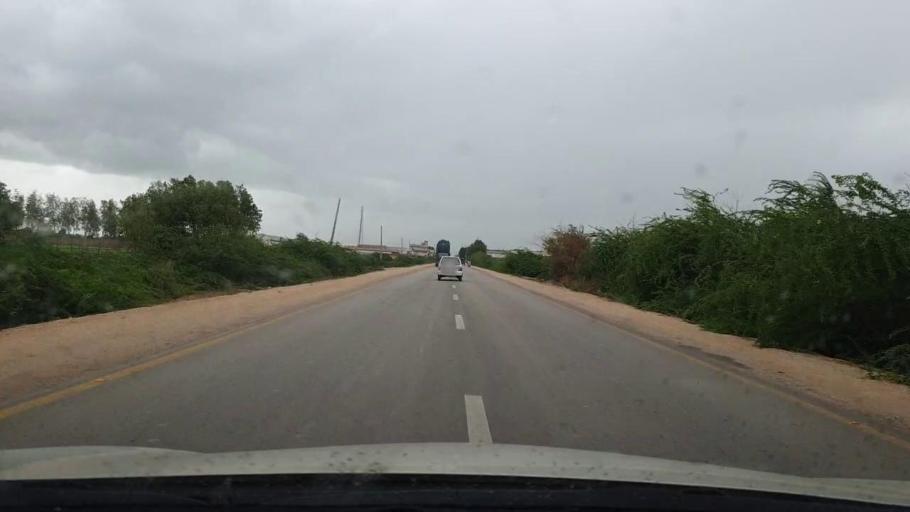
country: PK
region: Sindh
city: Kario
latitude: 24.6530
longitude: 68.5191
